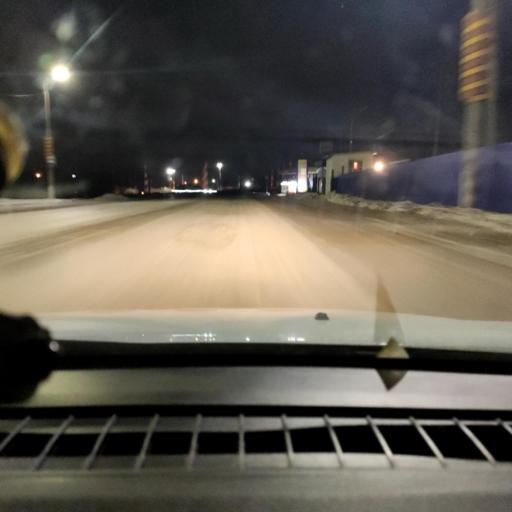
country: RU
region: Samara
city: Novokuybyshevsk
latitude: 53.0794
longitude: 49.9620
